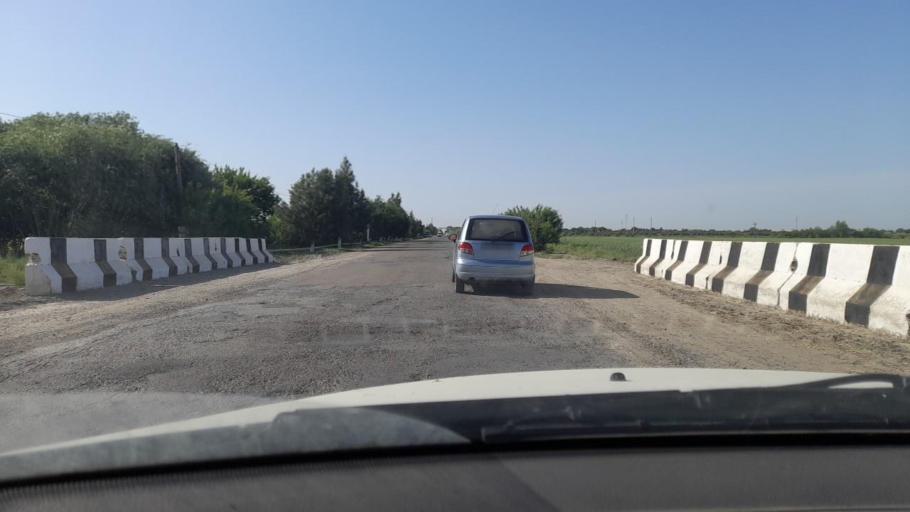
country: UZ
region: Bukhara
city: Romiton
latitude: 40.0719
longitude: 64.3265
